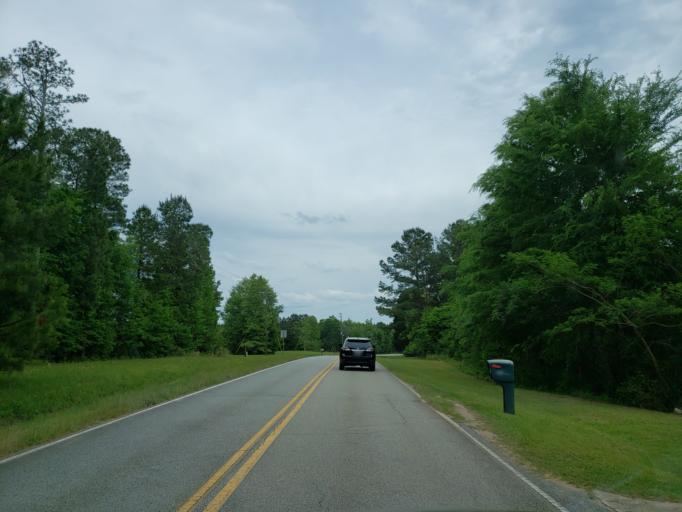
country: US
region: Georgia
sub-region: Bibb County
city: West Point
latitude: 32.8154
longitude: -83.8537
